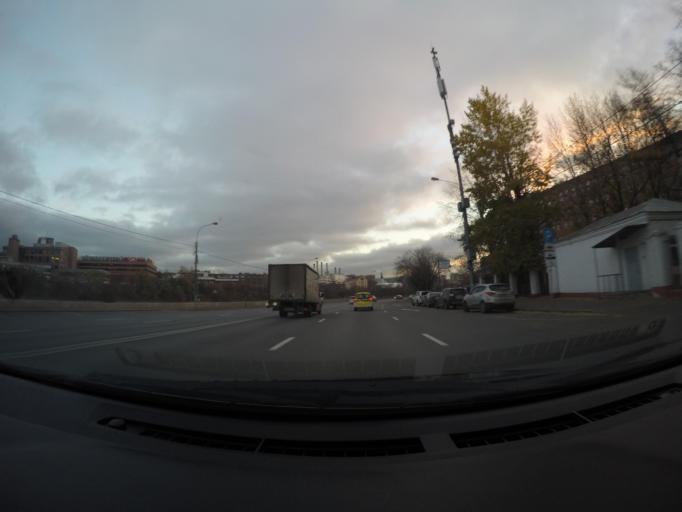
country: RU
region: Moskovskaya
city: Kozhukhovo
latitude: 55.7110
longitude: 37.6486
